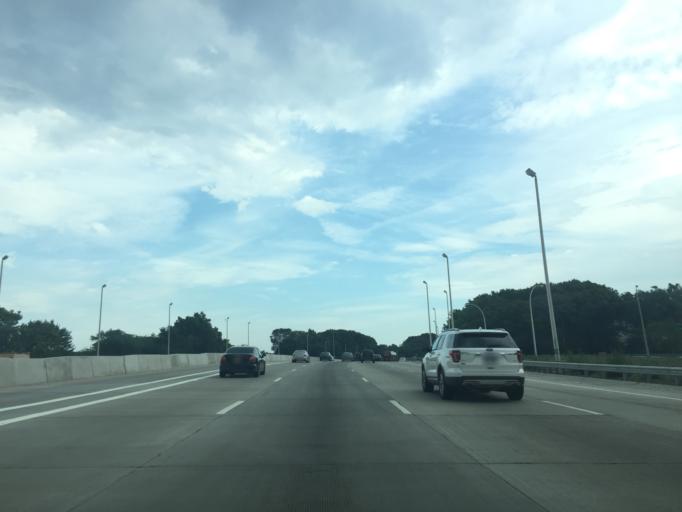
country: US
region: New York
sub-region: Richmond County
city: Staten Island
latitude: 40.6106
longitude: -74.1184
